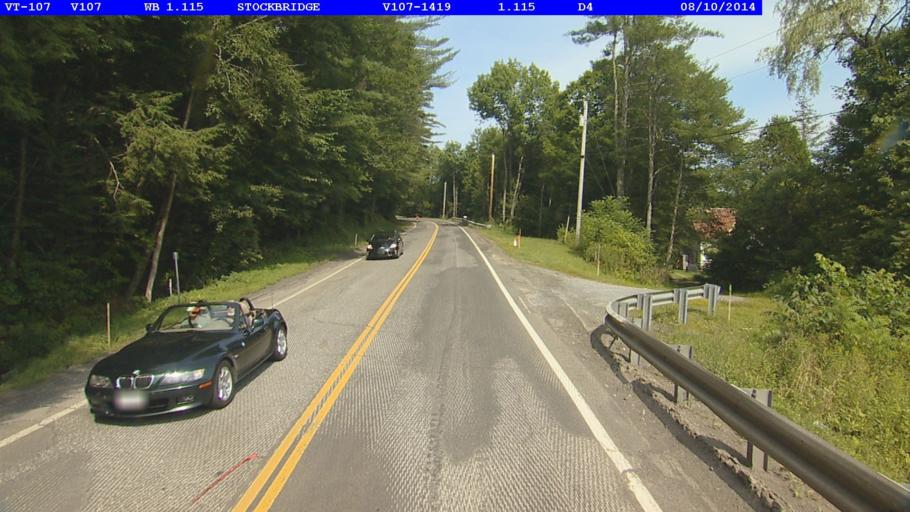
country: US
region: Vermont
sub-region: Orange County
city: Randolph
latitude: 43.7663
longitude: -72.7447
